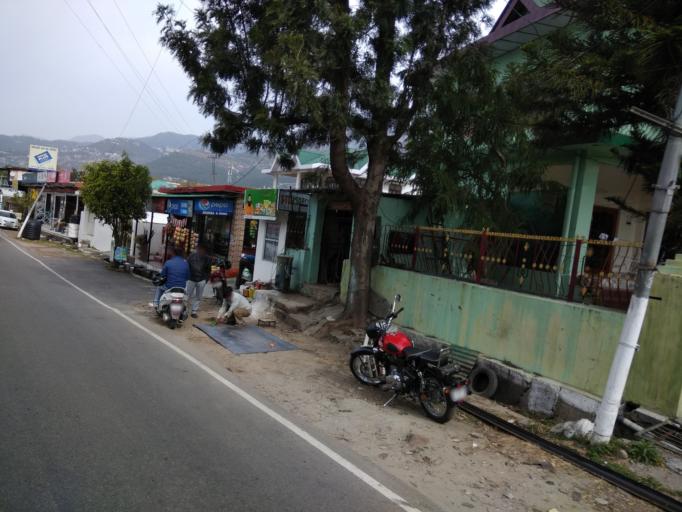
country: IN
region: Himachal Pradesh
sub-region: Kangra
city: Dharmsala
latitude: 32.1917
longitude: 76.3498
